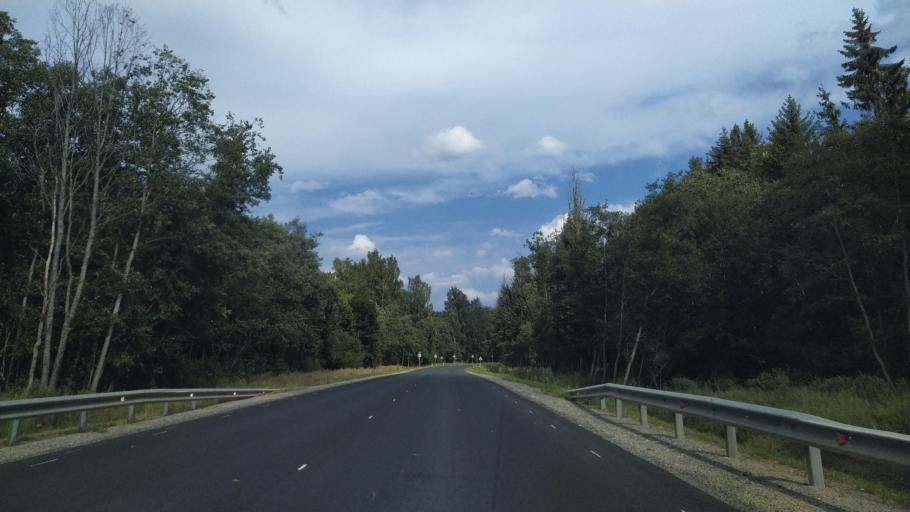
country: RU
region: Pskov
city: Vybor
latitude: 57.7127
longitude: 28.9192
